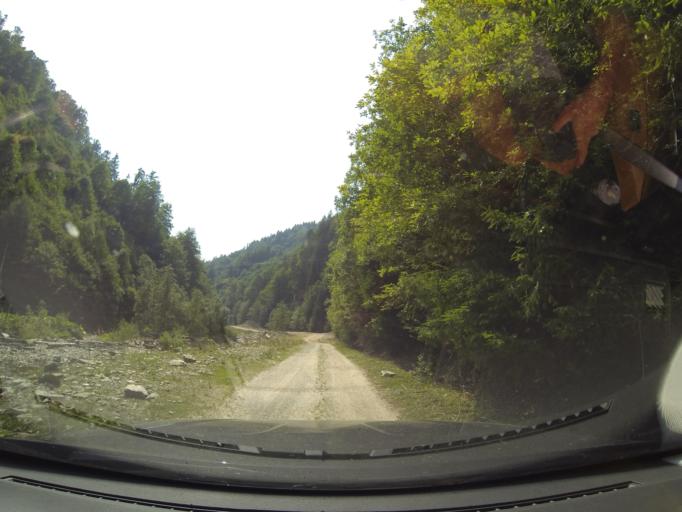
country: RO
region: Arges
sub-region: Comuna Arefu
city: Arefu
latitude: 45.4915
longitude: 24.6386
